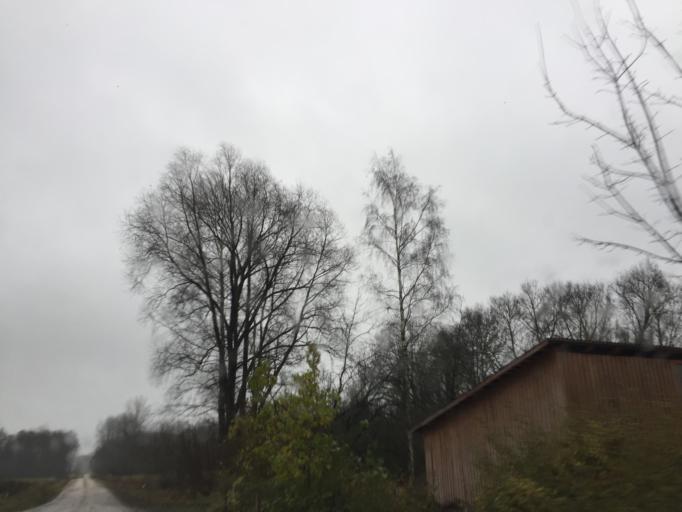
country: LV
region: Viesite
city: Viesite
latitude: 56.4614
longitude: 25.4879
